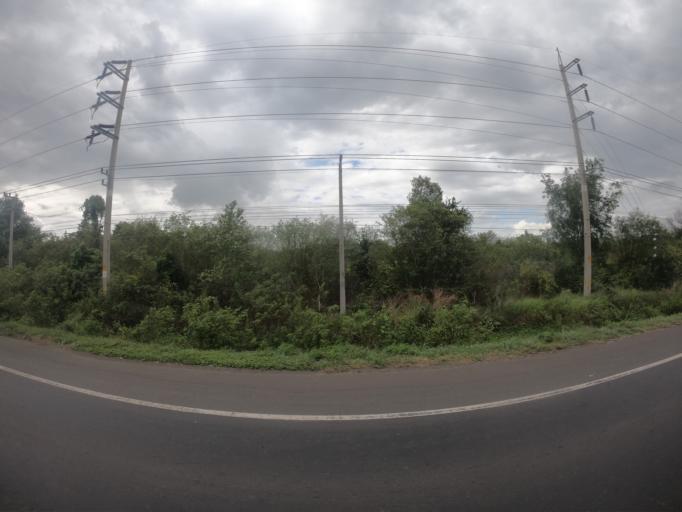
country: TH
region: Buriram
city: Prakhon Chai
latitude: 14.6092
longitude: 103.0415
